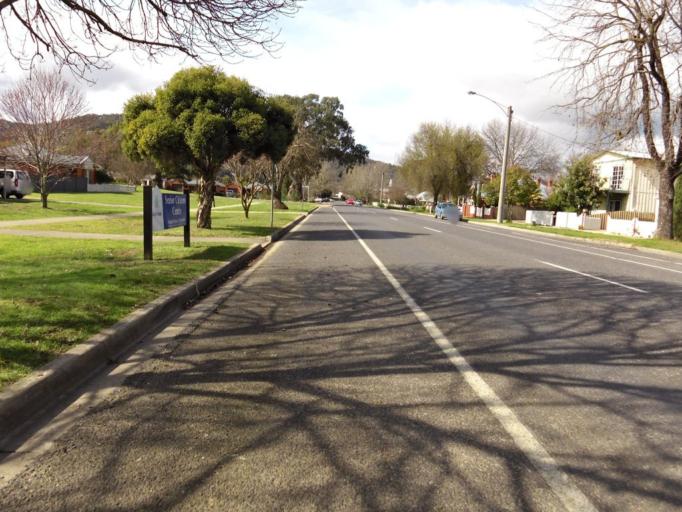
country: AU
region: Victoria
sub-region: Wangaratta
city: Wangaratta
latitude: -36.5580
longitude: 146.7217
